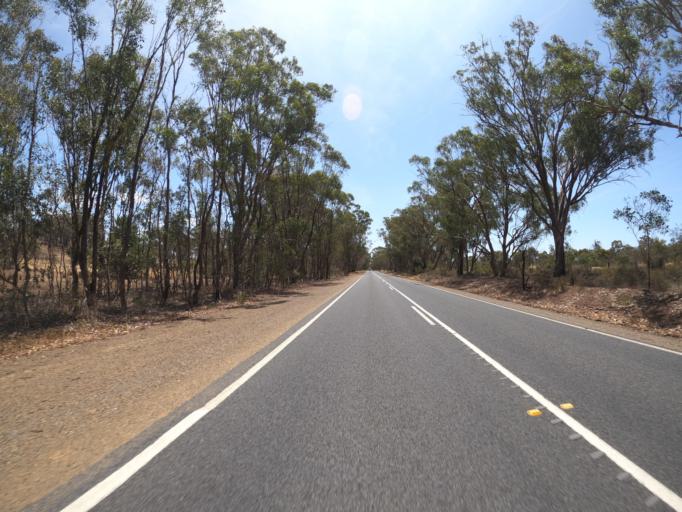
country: AU
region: Victoria
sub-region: Benalla
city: Benalla
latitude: -36.3720
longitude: 145.9729
